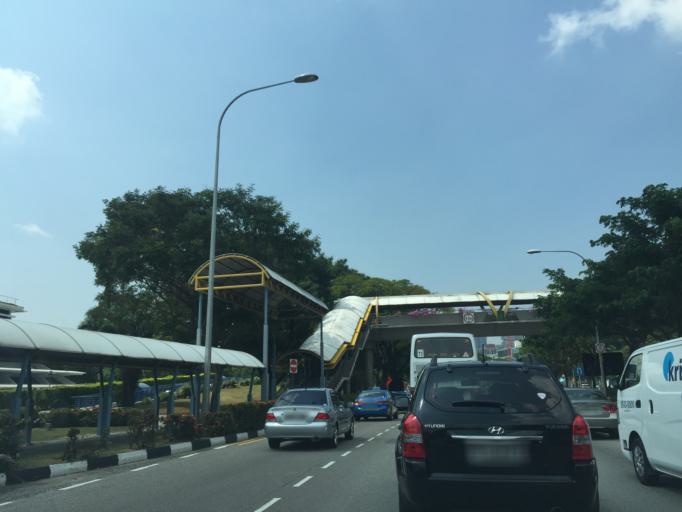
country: SG
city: Singapore
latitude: 1.3097
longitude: 103.8460
